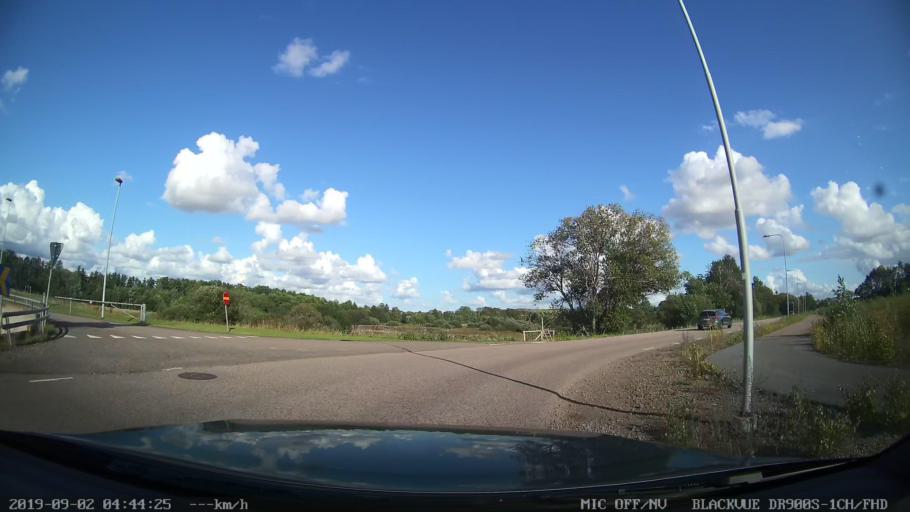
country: SE
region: Skane
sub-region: Helsingborg
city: Odakra
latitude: 56.0784
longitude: 12.7455
